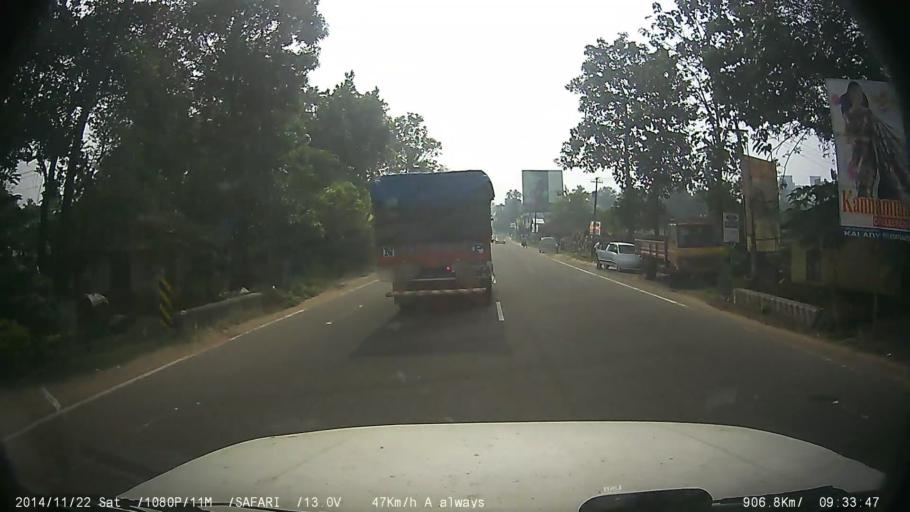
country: IN
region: Kerala
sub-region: Ernakulam
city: Angamali
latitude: 10.1735
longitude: 76.4253
